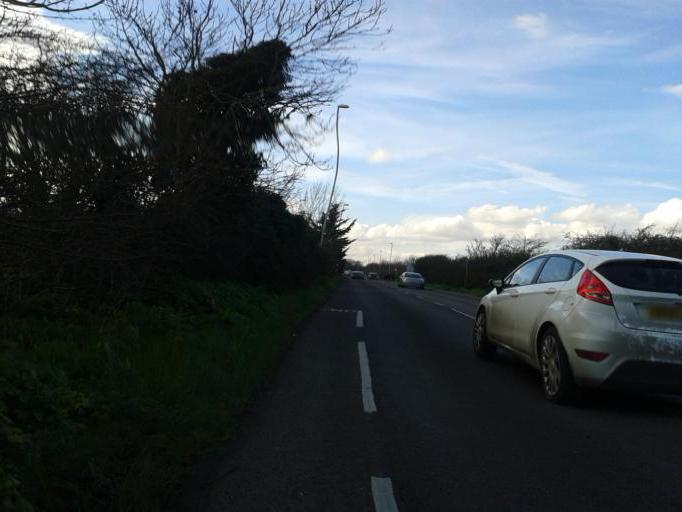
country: GB
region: England
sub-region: Cambridgeshire
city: Fulbourn
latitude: 52.1829
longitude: 0.1835
